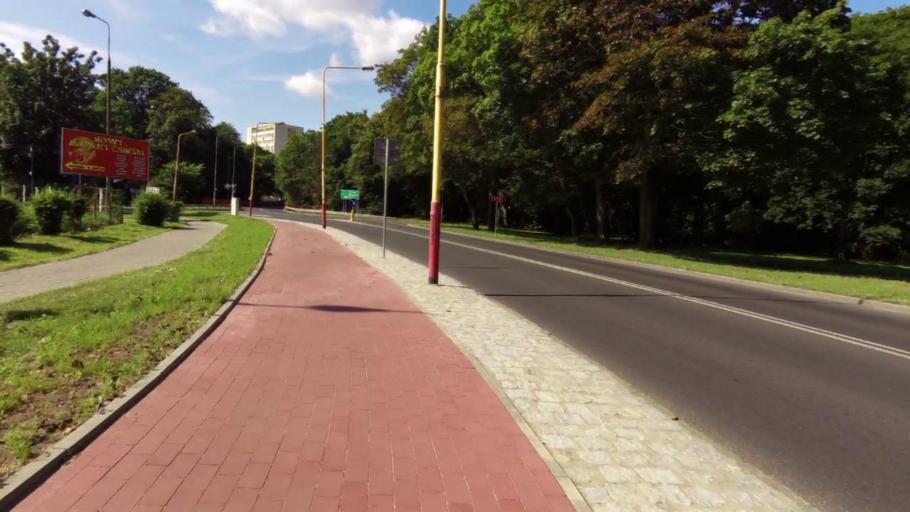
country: PL
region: West Pomeranian Voivodeship
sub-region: Powiat stargardzki
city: Stargard Szczecinski
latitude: 53.3425
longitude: 15.0509
